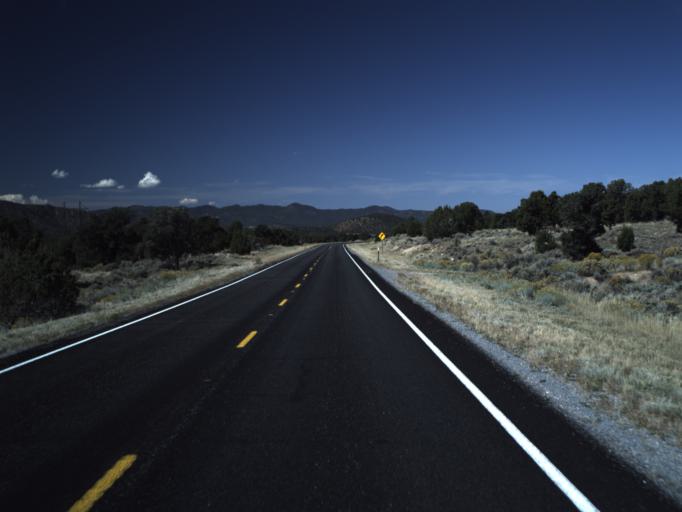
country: US
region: Utah
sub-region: Washington County
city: Enterprise
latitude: 37.6112
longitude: -113.3942
